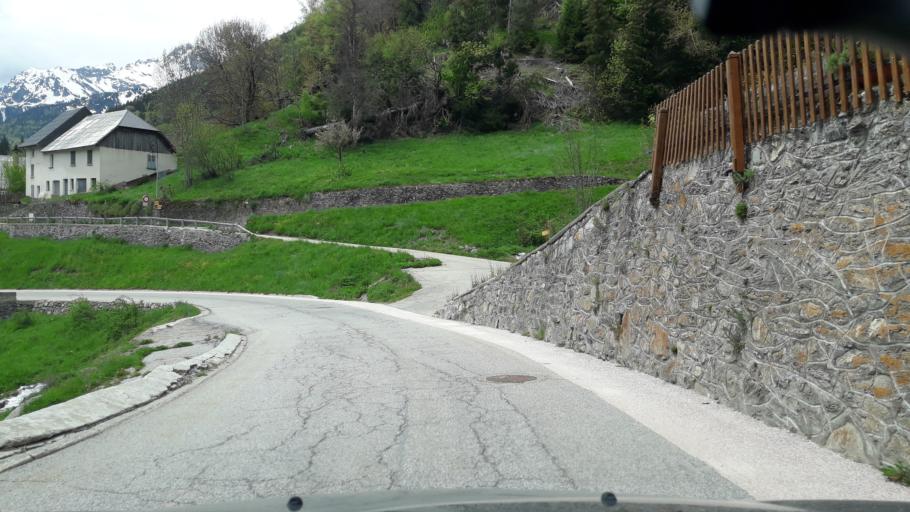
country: FR
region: Rhone-Alpes
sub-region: Departement de l'Isere
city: Theys
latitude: 45.2034
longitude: 6.0405
